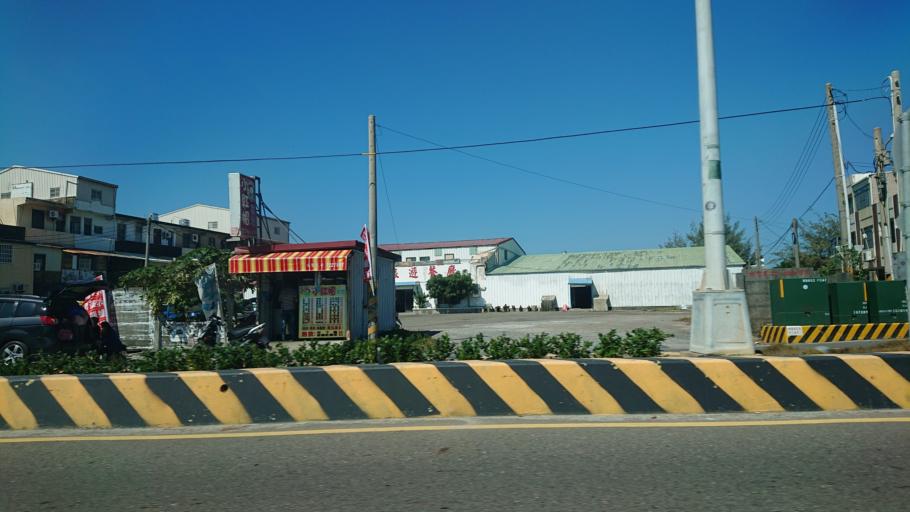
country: TW
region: Taiwan
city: Xinying
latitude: 23.2846
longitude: 120.1376
